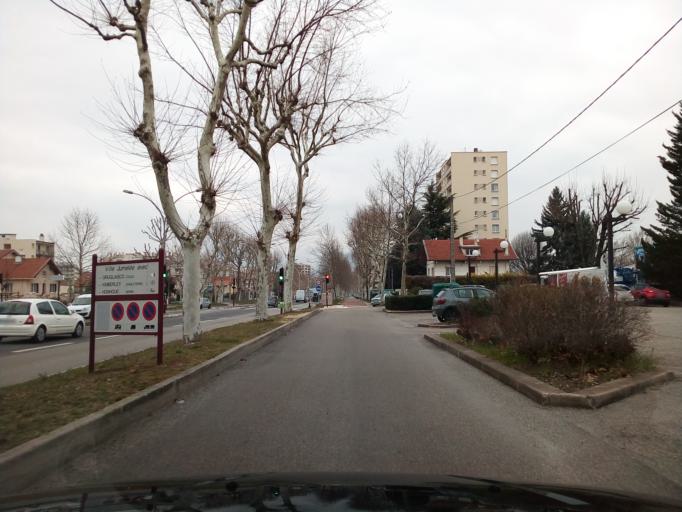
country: FR
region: Rhone-Alpes
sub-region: Departement de l'Isere
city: Le Pont-de-Claix
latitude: 45.1404
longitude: 5.7032
